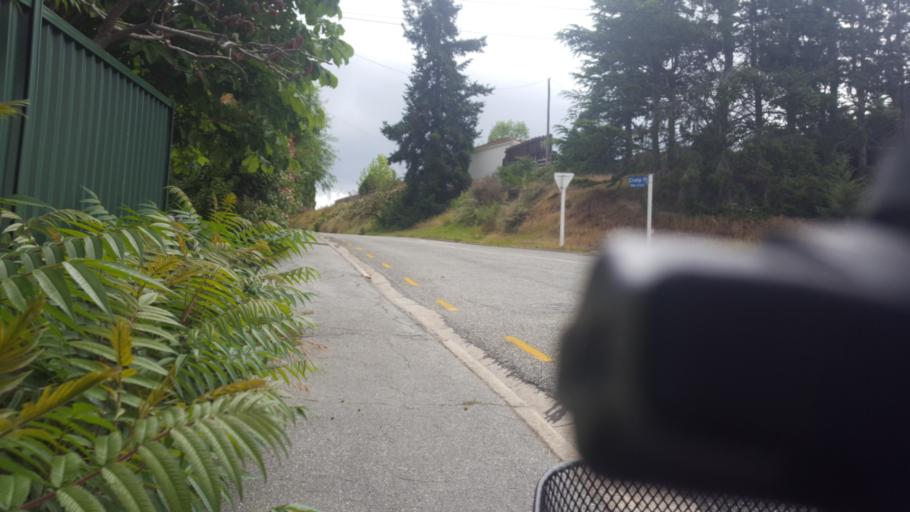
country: NZ
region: Otago
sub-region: Queenstown-Lakes District
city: Wanaka
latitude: -45.2604
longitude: 169.3825
